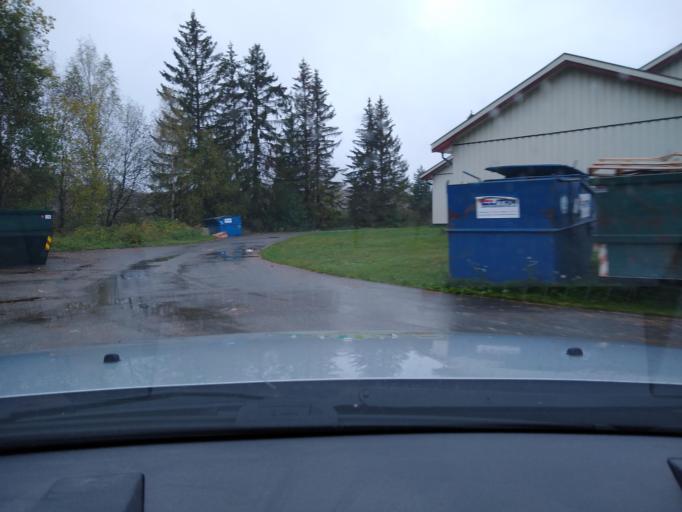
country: NO
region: Oppland
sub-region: Ringebu
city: Ringebu
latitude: 61.5408
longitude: 10.0532
